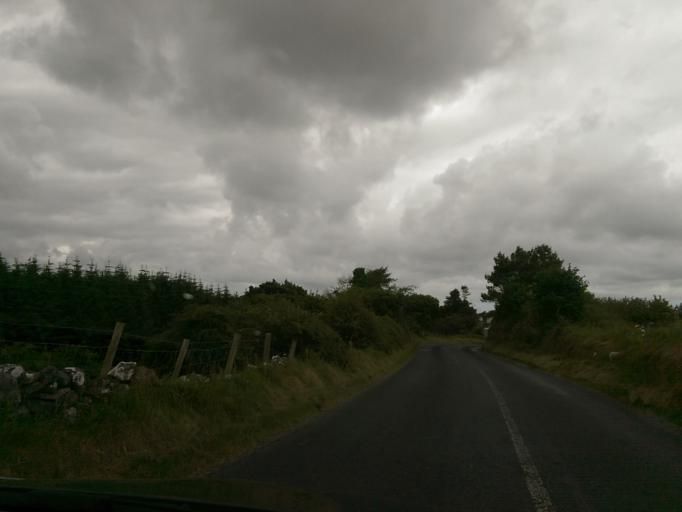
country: IE
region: Connaught
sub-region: County Galway
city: Loughrea
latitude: 53.2929
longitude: -8.5093
